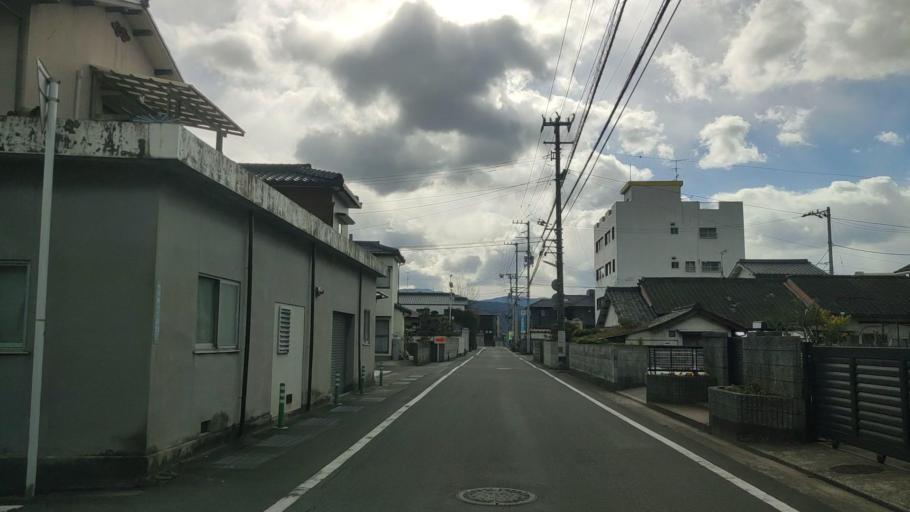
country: JP
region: Ehime
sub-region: Shikoku-chuo Shi
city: Matsuyama
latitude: 33.8108
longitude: 132.7525
